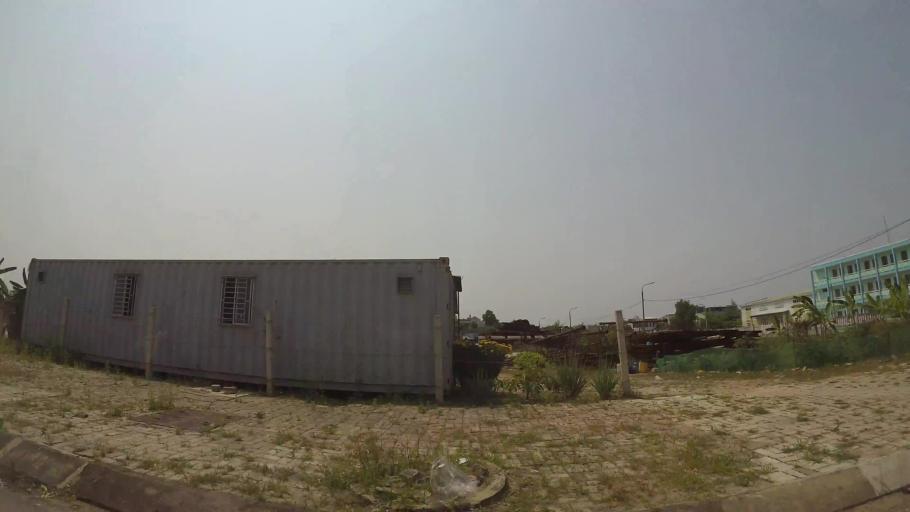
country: VN
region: Da Nang
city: Cam Le
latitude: 15.9896
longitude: 108.2110
